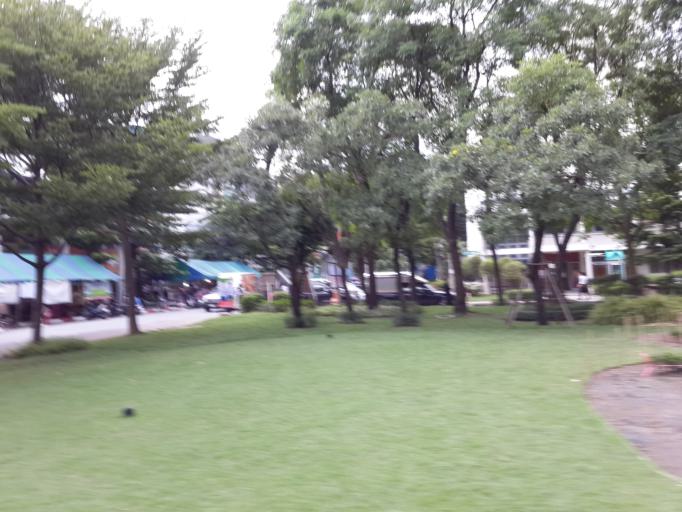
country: TH
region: Bangkok
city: Lak Si
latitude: 13.8763
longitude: 100.5902
